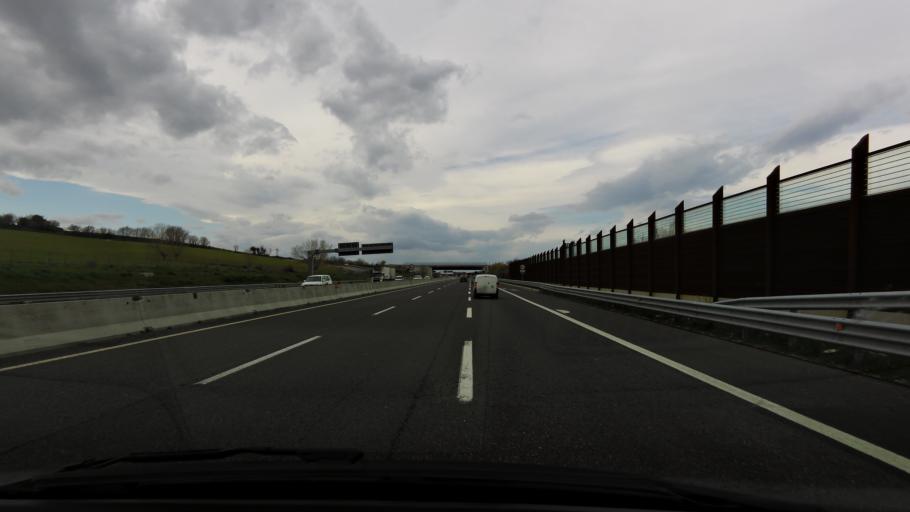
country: IT
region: The Marches
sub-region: Provincia di Pesaro e Urbino
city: Marotta
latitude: 43.7650
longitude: 13.1267
